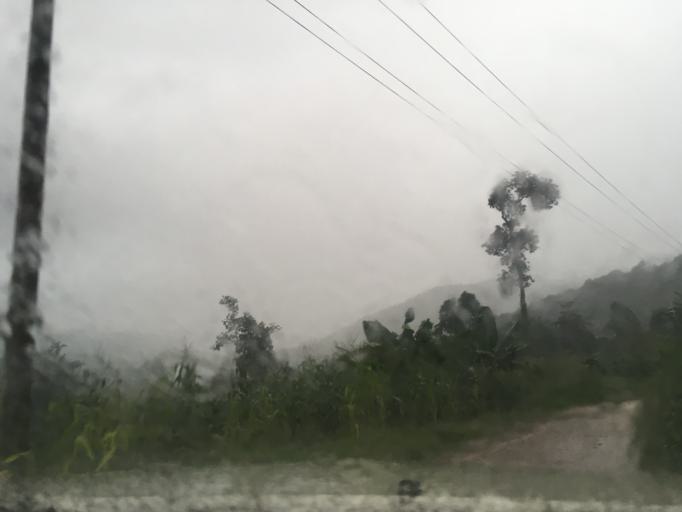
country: LA
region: Oudomxai
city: Muang La
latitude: 21.2382
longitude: 101.9557
